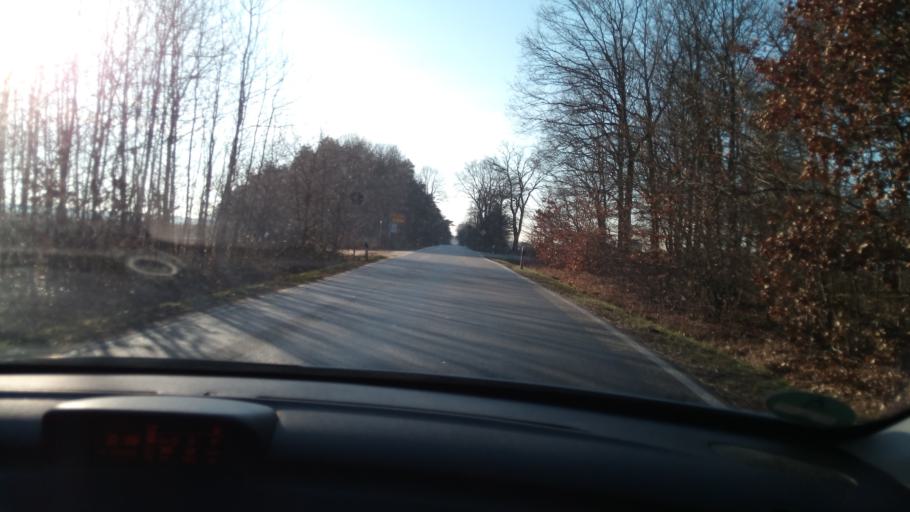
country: DE
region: Schleswig-Holstein
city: Besenthal
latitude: 53.5353
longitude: 10.7257
